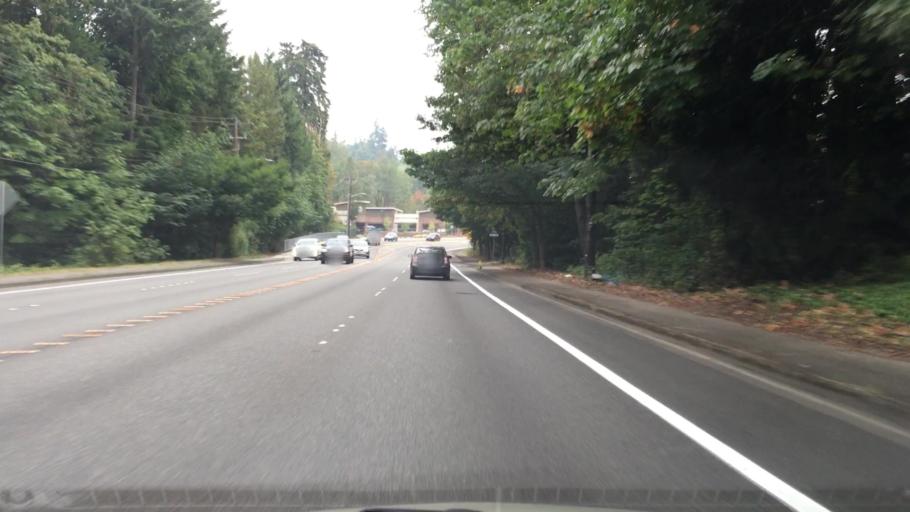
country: US
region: Washington
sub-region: King County
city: Newcastle
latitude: 47.5456
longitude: -122.1657
